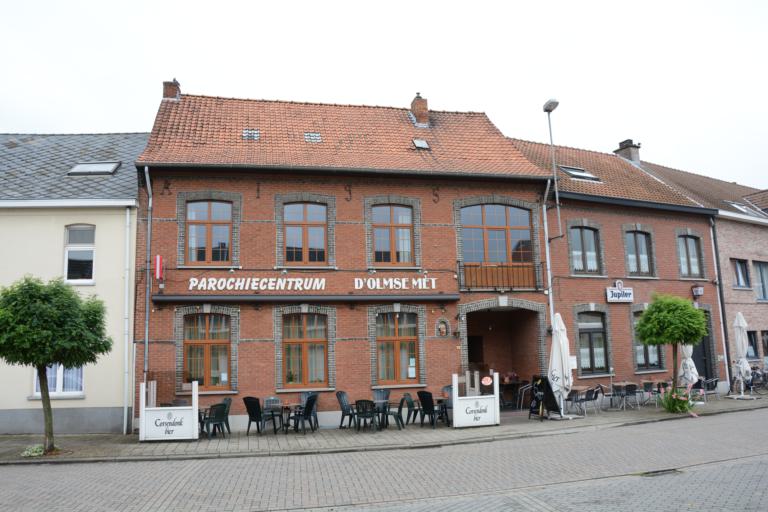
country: BE
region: Flanders
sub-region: Provincie Antwerpen
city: Balen
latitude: 51.1420
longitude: 5.1502
